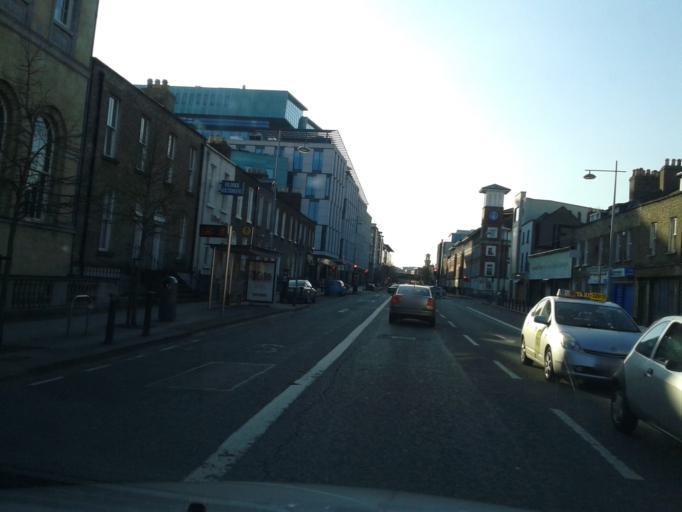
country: IE
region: Leinster
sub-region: Dublin City
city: Dublin
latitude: 53.3432
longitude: -6.2450
